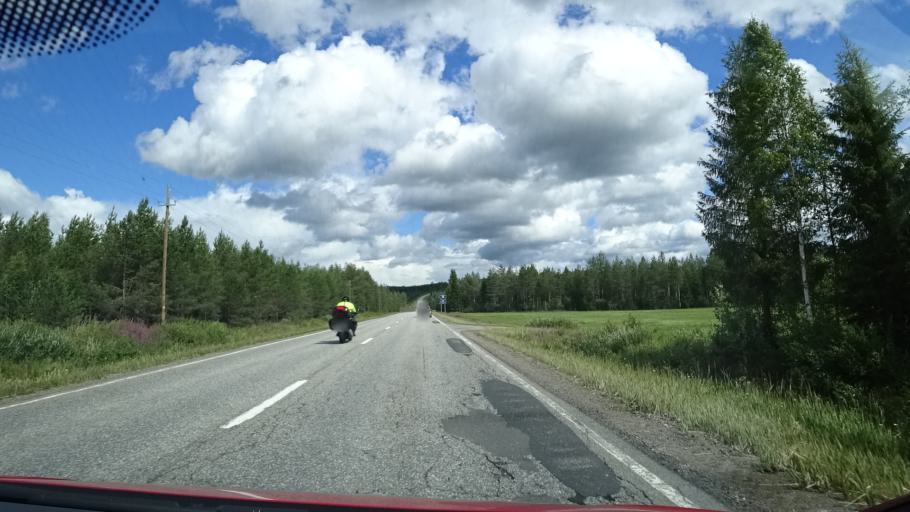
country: FI
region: Northern Savo
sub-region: Koillis-Savo
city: Rautavaara
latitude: 63.3330
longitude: 28.4407
